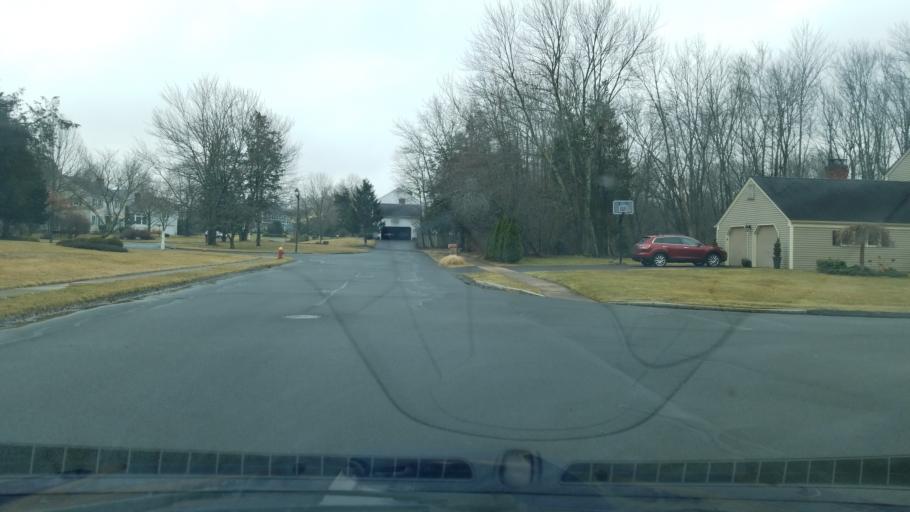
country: US
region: Connecticut
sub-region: Hartford County
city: Wethersfield
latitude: 41.6736
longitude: -72.6804
